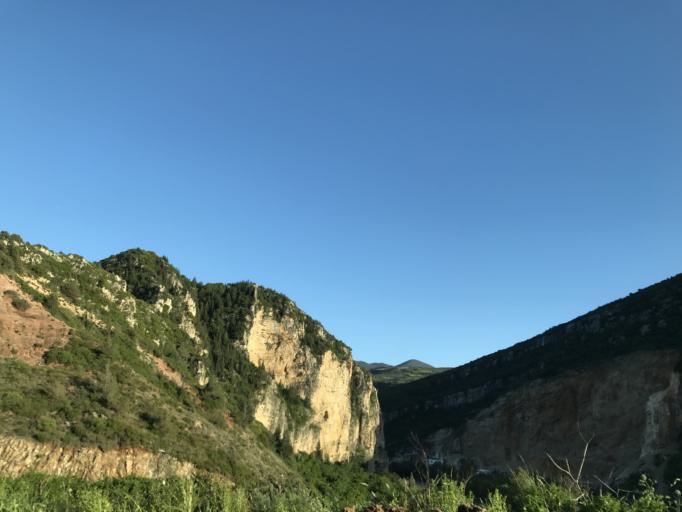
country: TR
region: Hatay
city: Samandag
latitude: 36.0754
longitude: 36.0291
